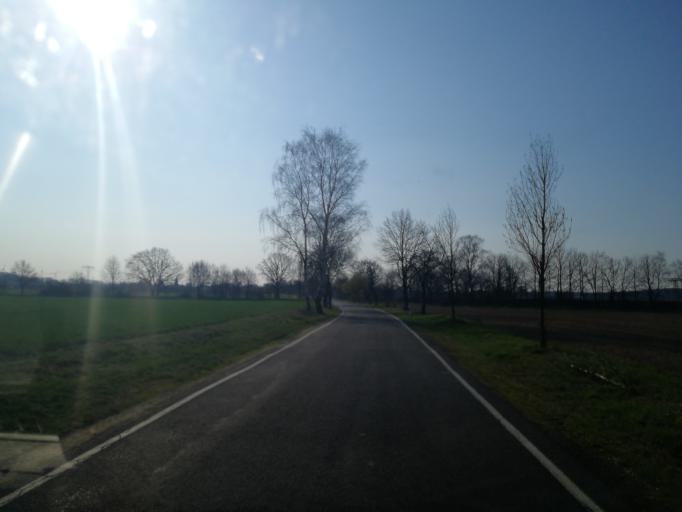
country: DE
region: Brandenburg
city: Drahnsdorf
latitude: 51.8597
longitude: 13.5962
